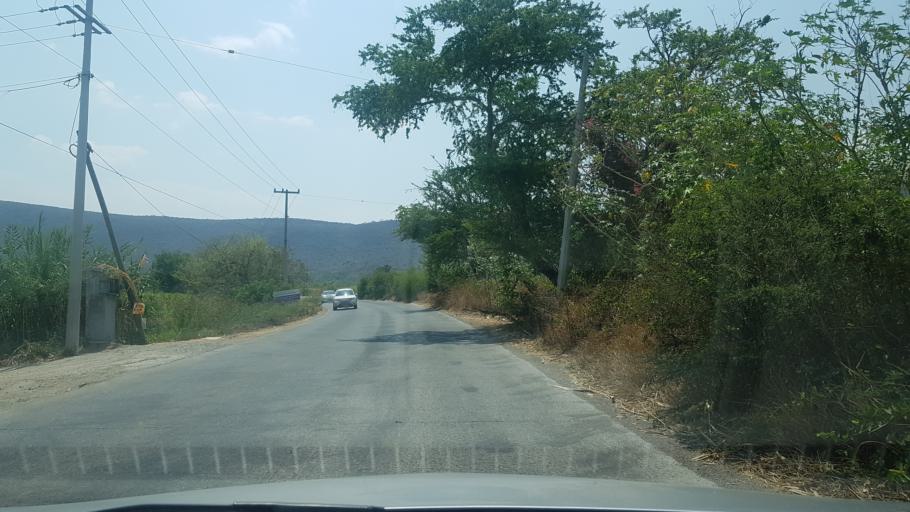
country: MX
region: Morelos
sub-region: Tlaltizapan de Zapata
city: Colonia Palo Prieto (Chipitongo)
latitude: 18.7324
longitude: -99.1169
